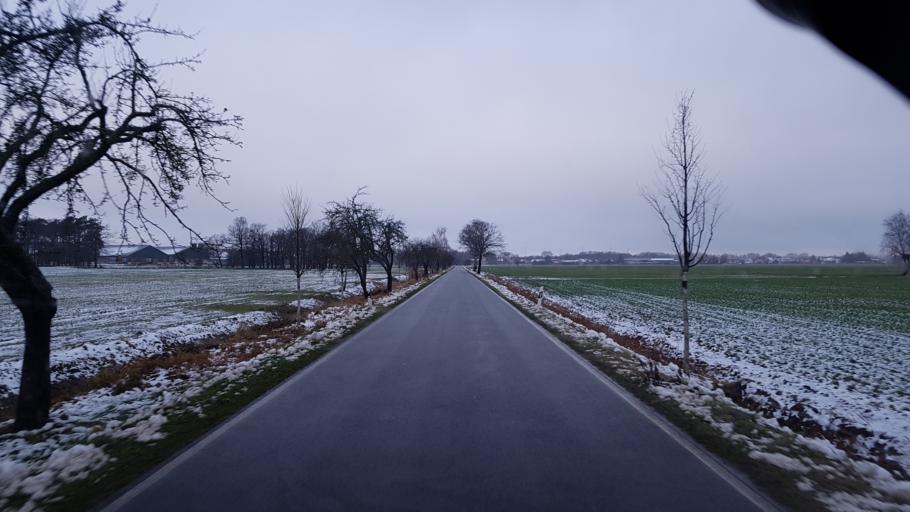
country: DE
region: Brandenburg
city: Luckau
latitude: 51.8124
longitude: 13.7082
